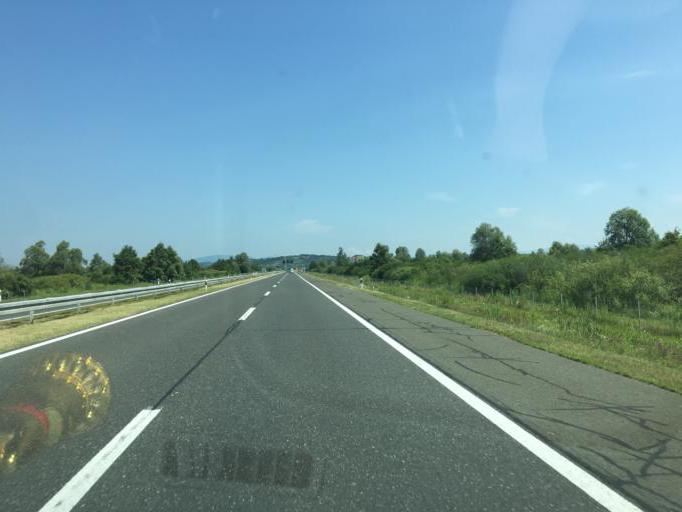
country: HR
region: Zagrebacka
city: Jakovlje
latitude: 45.9887
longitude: 15.8598
